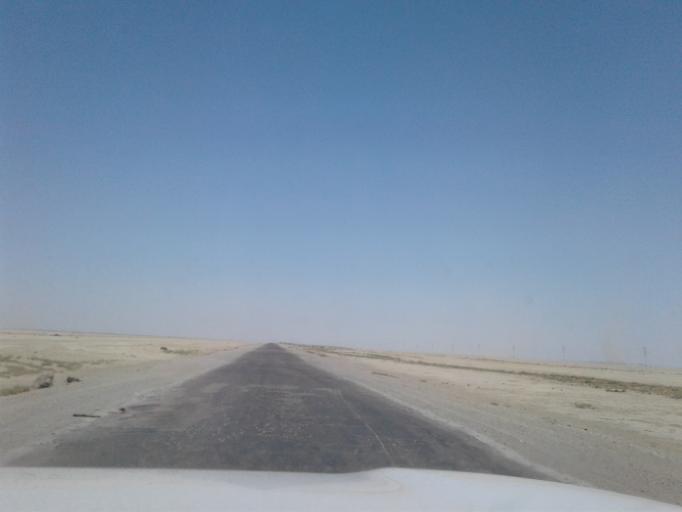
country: TM
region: Balkan
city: Gumdag
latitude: 38.7379
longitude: 54.5142
